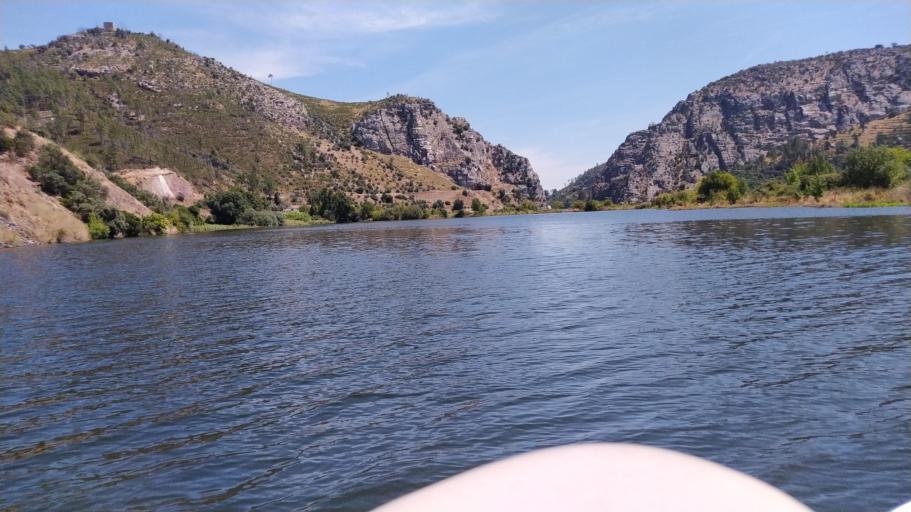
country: PT
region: Portalegre
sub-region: Nisa
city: Nisa
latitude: 39.6414
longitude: -7.6972
